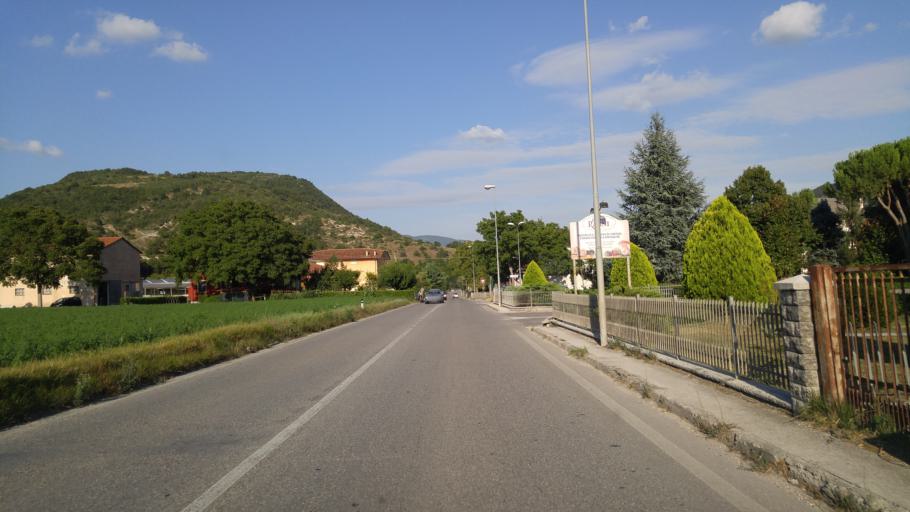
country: IT
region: The Marches
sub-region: Provincia di Pesaro e Urbino
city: Acqualagna
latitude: 43.6134
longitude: 12.6340
